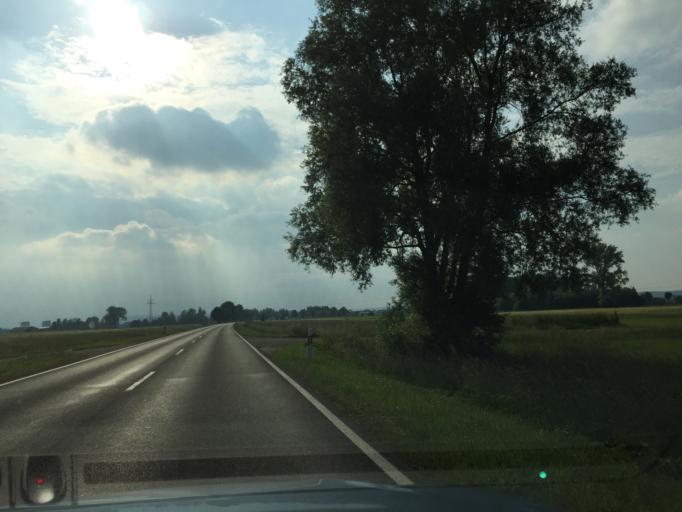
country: DE
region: Bavaria
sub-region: Swabia
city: Senden
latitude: 48.3703
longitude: 10.0548
